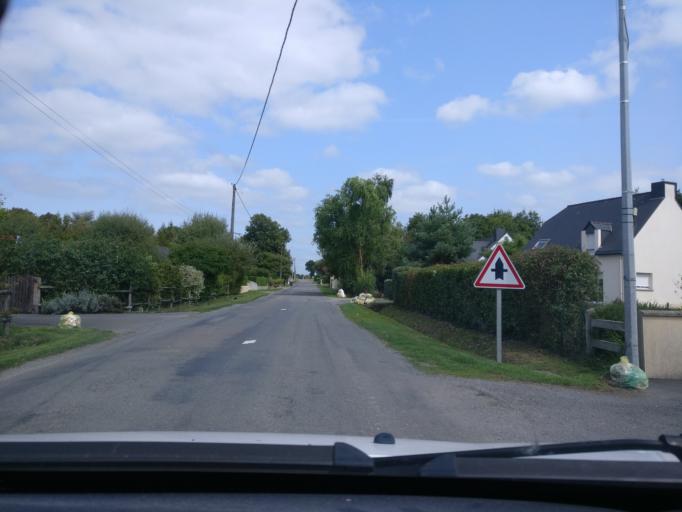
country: FR
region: Brittany
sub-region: Departement d'Ille-et-Vilaine
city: Saint-Sulpice-la-Foret
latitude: 48.2328
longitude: -1.5863
